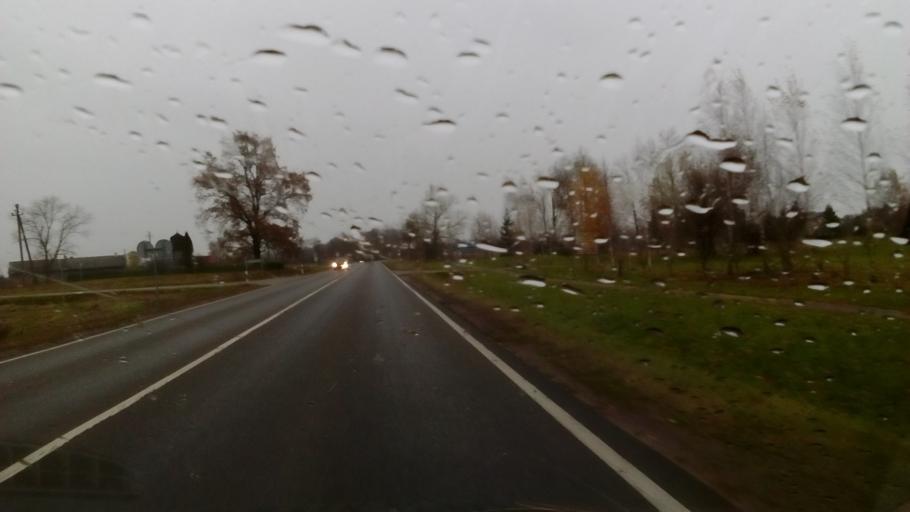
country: LT
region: Marijampoles apskritis
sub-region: Marijampole Municipality
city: Marijampole
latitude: 54.5496
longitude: 23.4049
